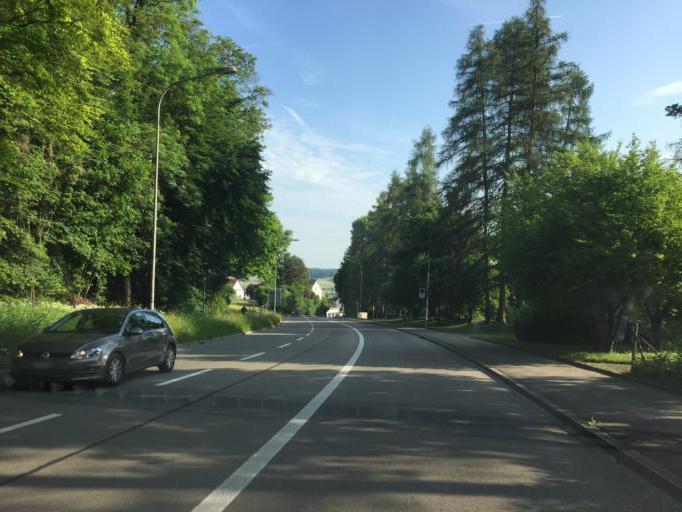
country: CH
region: Zurich
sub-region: Bezirk Zuerich
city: Zuerich (Kreis 11) / Affoltern
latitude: 47.4139
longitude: 8.5064
